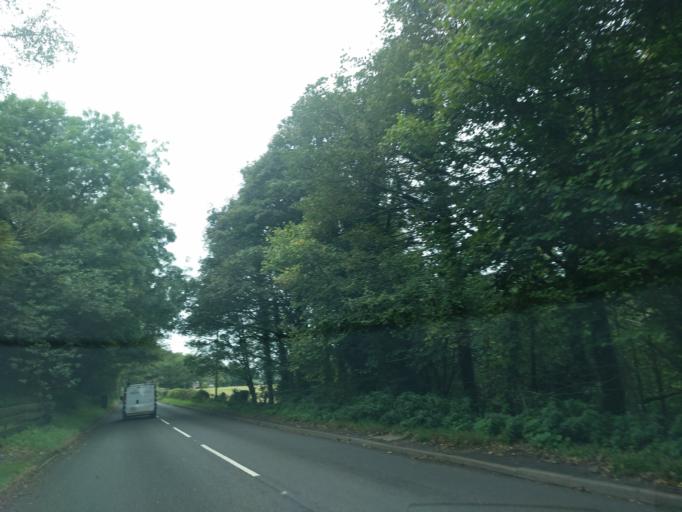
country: GB
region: England
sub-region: Staffordshire
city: Audley
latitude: 53.0146
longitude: -2.3400
